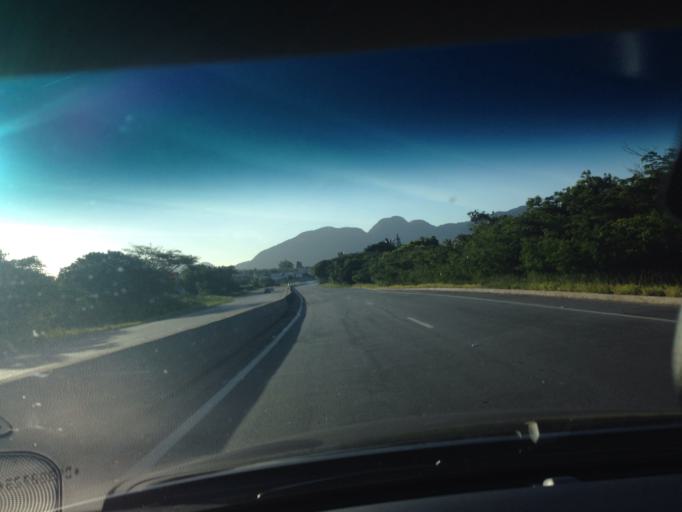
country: BR
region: Espirito Santo
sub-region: Guarapari
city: Guarapari
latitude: -20.6142
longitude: -40.4507
